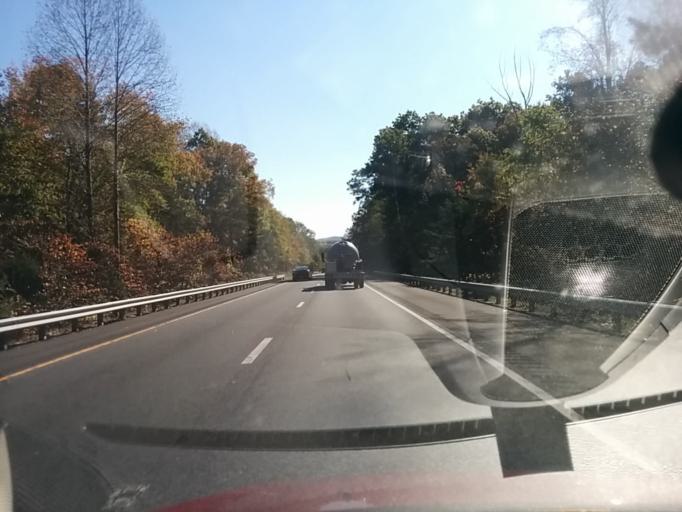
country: US
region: Virginia
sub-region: Albemarle County
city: Crozet
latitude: 38.0331
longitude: -78.6878
